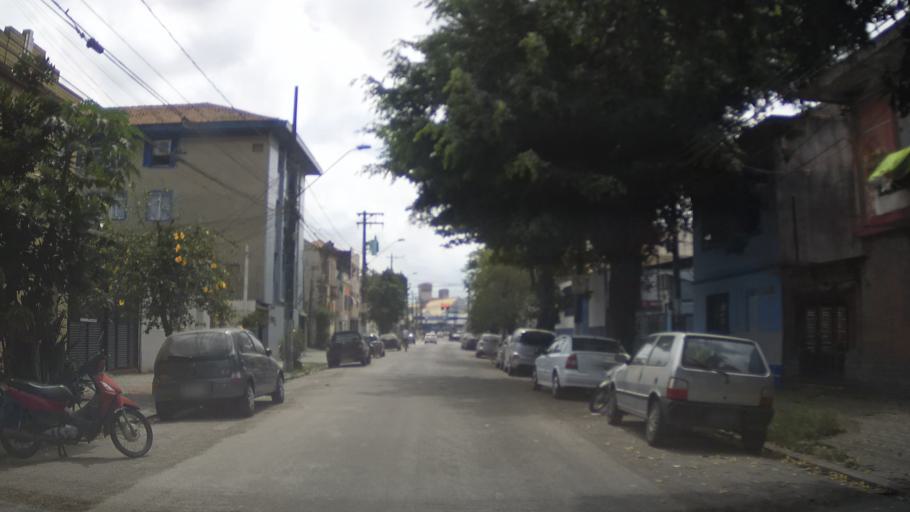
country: BR
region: Sao Paulo
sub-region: Santos
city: Santos
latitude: -23.9535
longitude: -46.3157
